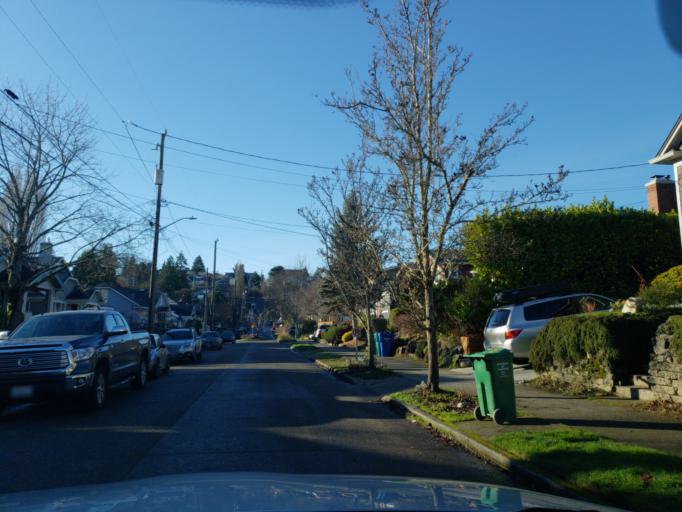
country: US
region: Washington
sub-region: King County
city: Seattle
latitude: 47.6796
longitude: -122.3488
